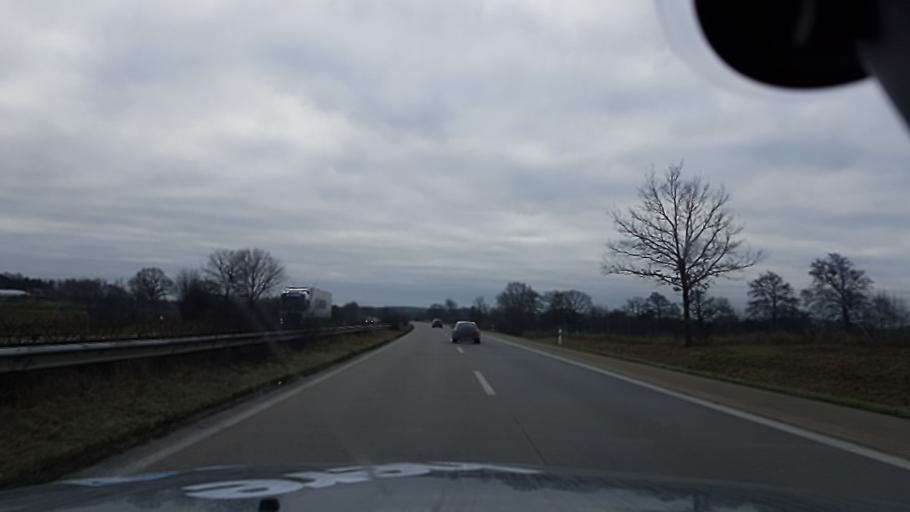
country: DE
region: Schleswig-Holstein
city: Ratekau
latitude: 53.9707
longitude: 10.7337
